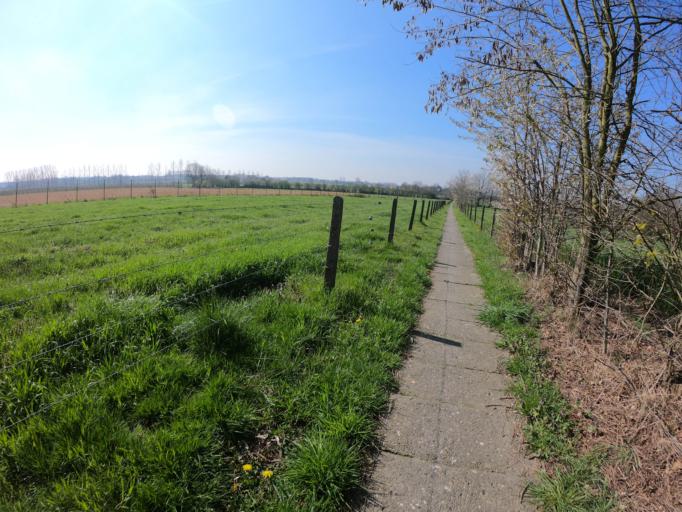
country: BE
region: Flanders
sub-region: Provincie Limburg
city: Herk-de-Stad
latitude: 50.9004
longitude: 5.1717
